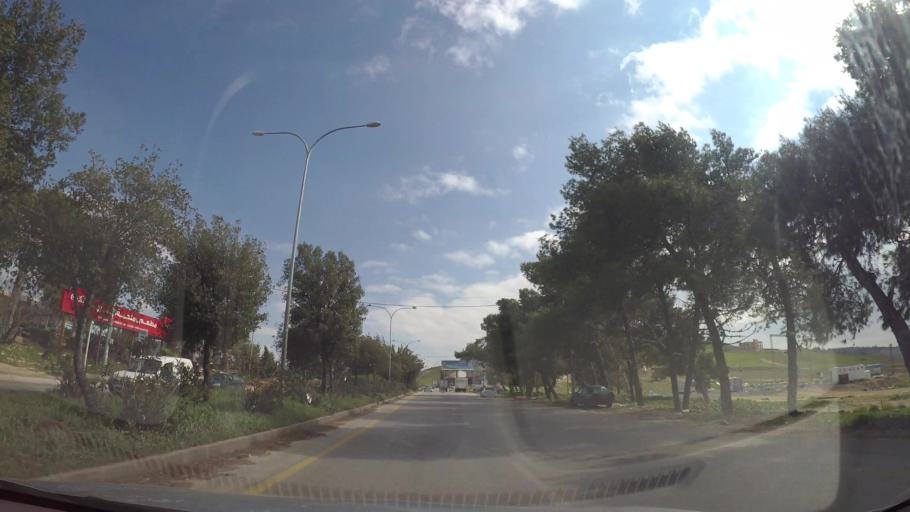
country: JO
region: Balqa
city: As Salt
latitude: 32.0363
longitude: 35.7906
